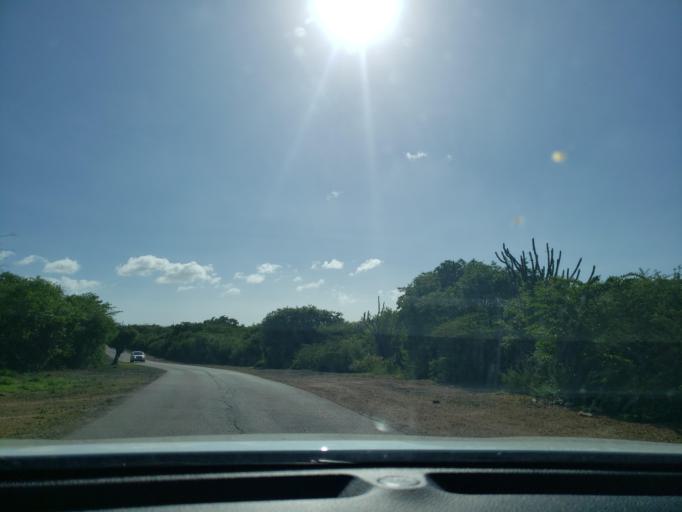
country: CW
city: Dorp Soto
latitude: 12.3496
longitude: -69.1524
